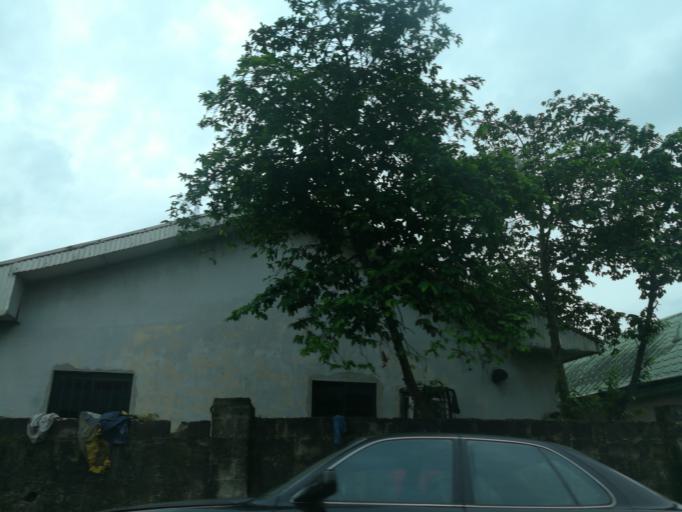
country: NG
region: Rivers
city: Port Harcourt
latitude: 4.8357
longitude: 7.0178
